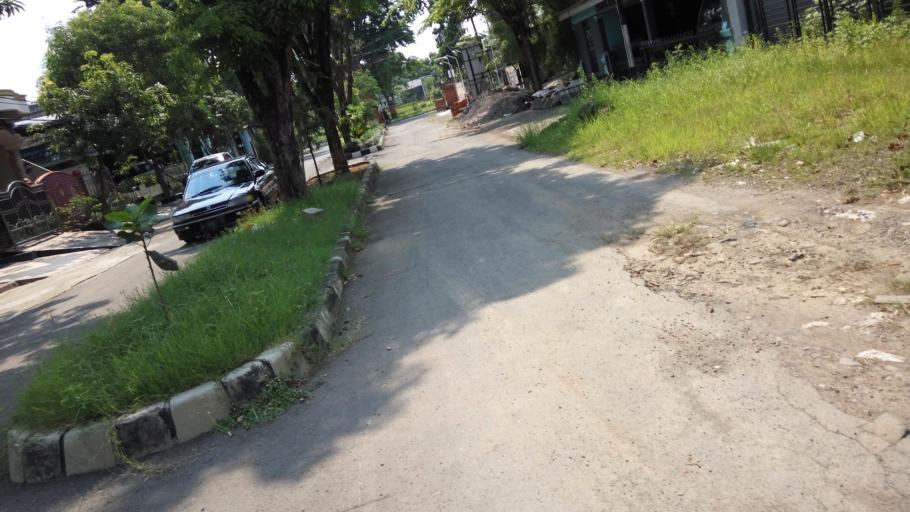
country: ID
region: Central Java
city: Mranggen
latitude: -7.0360
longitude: 110.4727
